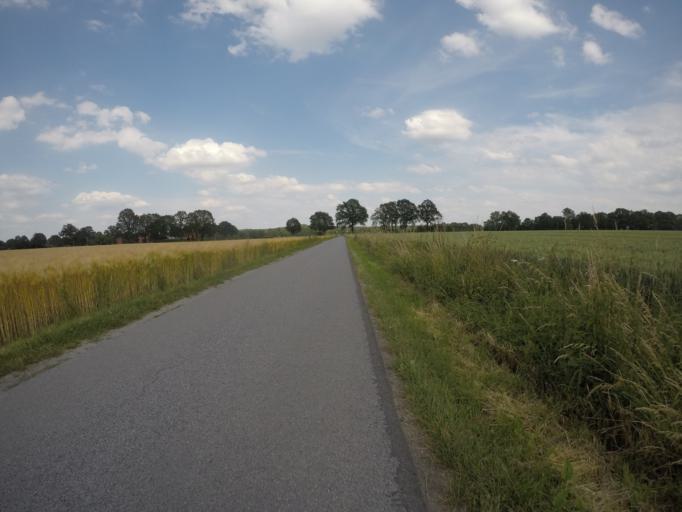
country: DE
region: North Rhine-Westphalia
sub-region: Regierungsbezirk Munster
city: Coesfeld
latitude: 51.8884
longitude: 7.1010
